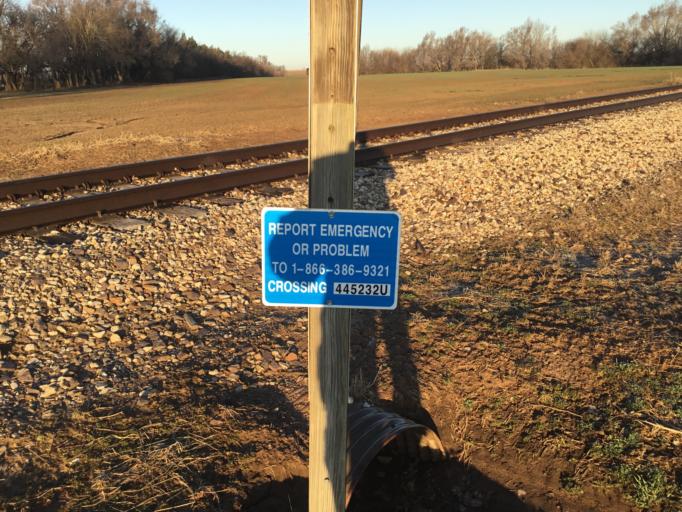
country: US
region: Kansas
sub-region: Sedgwick County
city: Saint Marys
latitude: 37.8007
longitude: -97.6448
